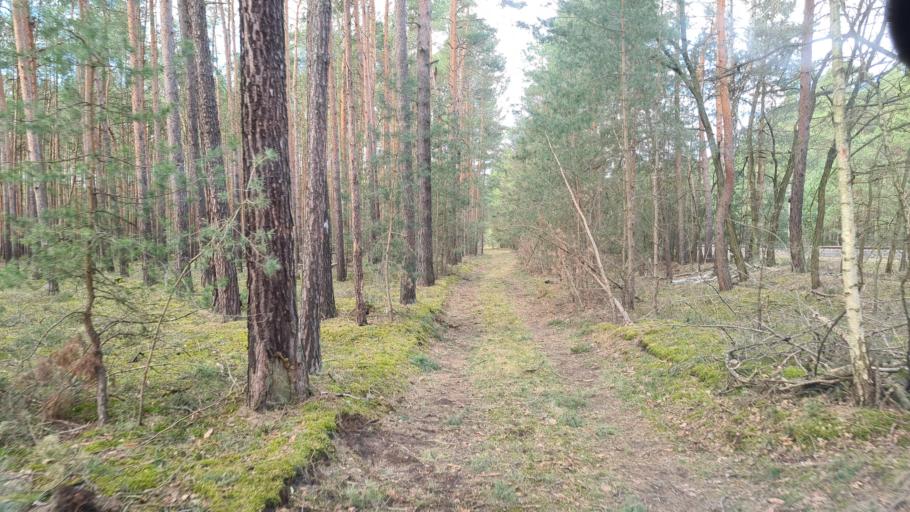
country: DE
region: Brandenburg
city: Bruck
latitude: 52.1692
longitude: 12.7240
